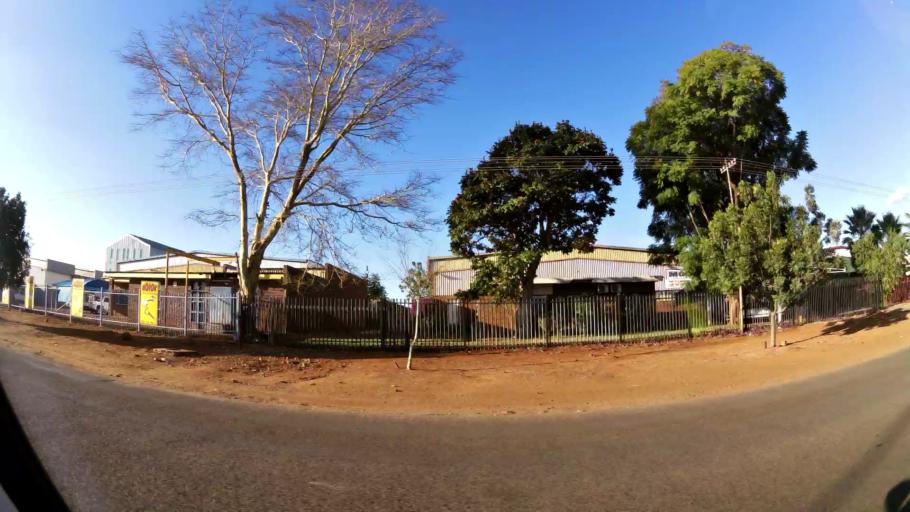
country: ZA
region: Limpopo
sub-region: Waterberg District Municipality
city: Mokopane
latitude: -24.1674
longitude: 28.9957
